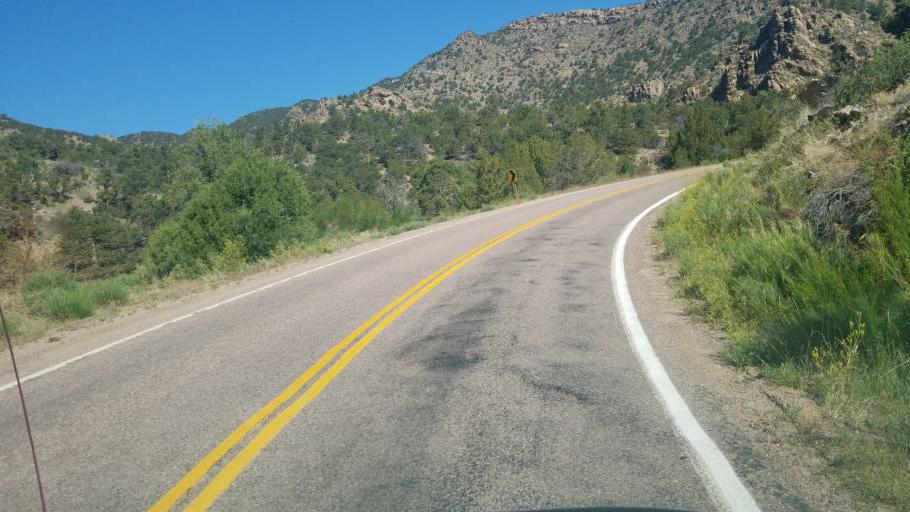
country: US
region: Colorado
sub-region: Fremont County
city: Canon City
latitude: 38.4313
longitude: -105.3924
